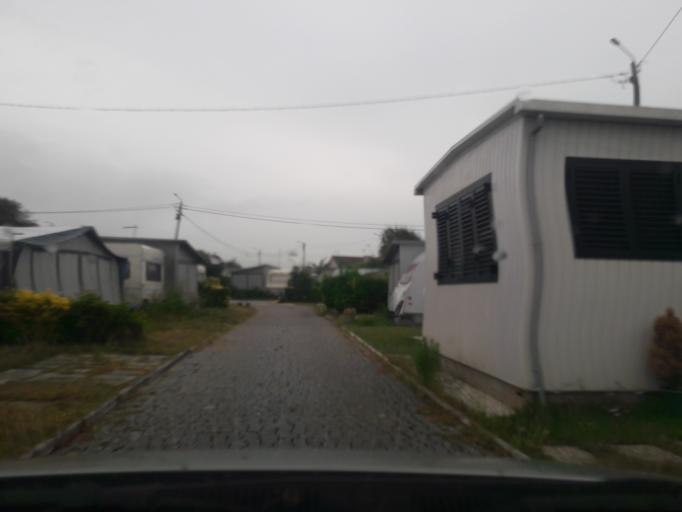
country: PT
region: Porto
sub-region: Vila do Conde
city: Vila do Conde
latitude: 41.3359
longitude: -8.7377
